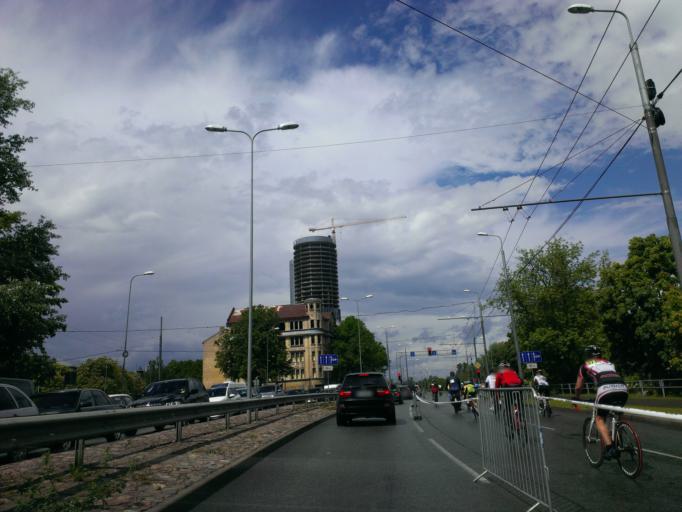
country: LV
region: Riga
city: Riga
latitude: 56.9439
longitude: 24.0851
